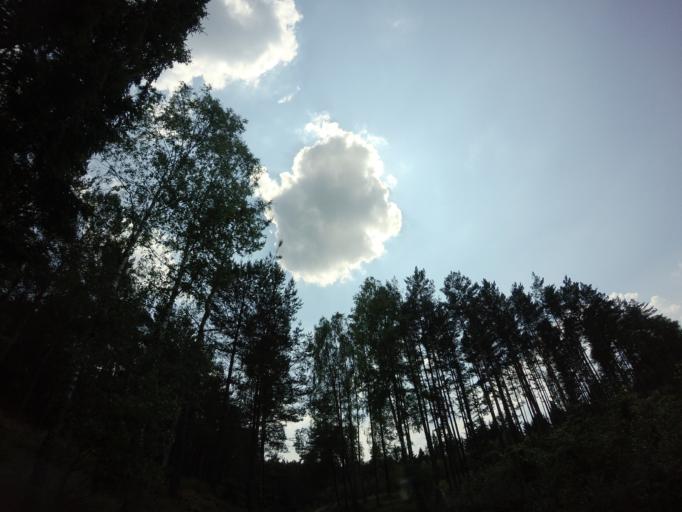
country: PL
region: West Pomeranian Voivodeship
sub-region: Powiat choszczenski
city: Bierzwnik
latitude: 53.0947
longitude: 15.7145
